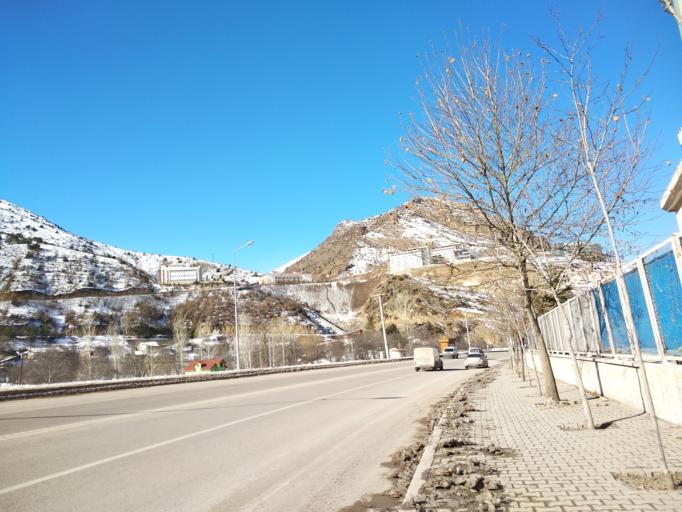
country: TR
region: Gumushane
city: Gumushkhane
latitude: 40.4372
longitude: 39.5065
